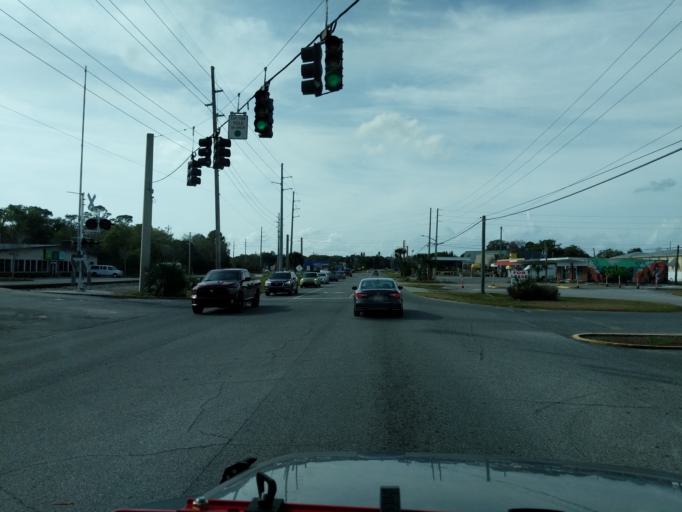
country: US
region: Florida
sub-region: Lake County
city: Mount Dora
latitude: 28.8077
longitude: -81.6730
